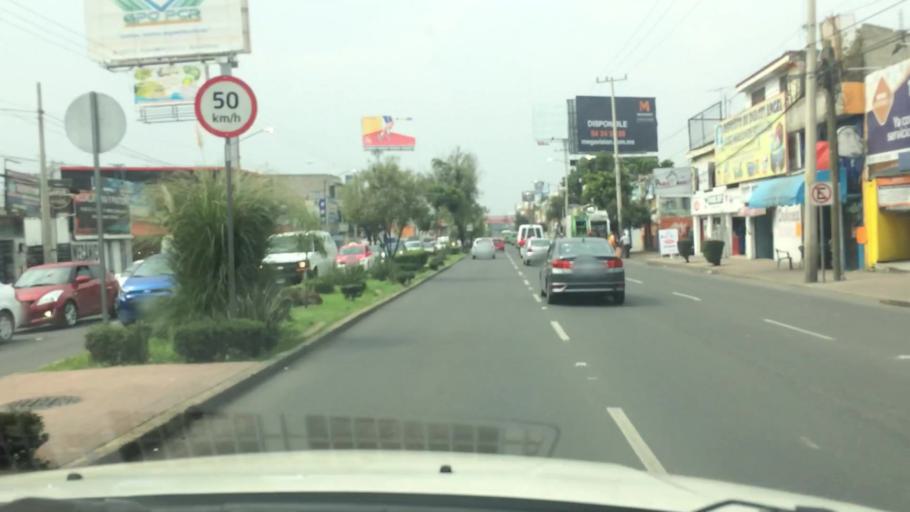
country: MX
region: Mexico City
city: Xochimilco
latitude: 19.2748
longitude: -99.1204
